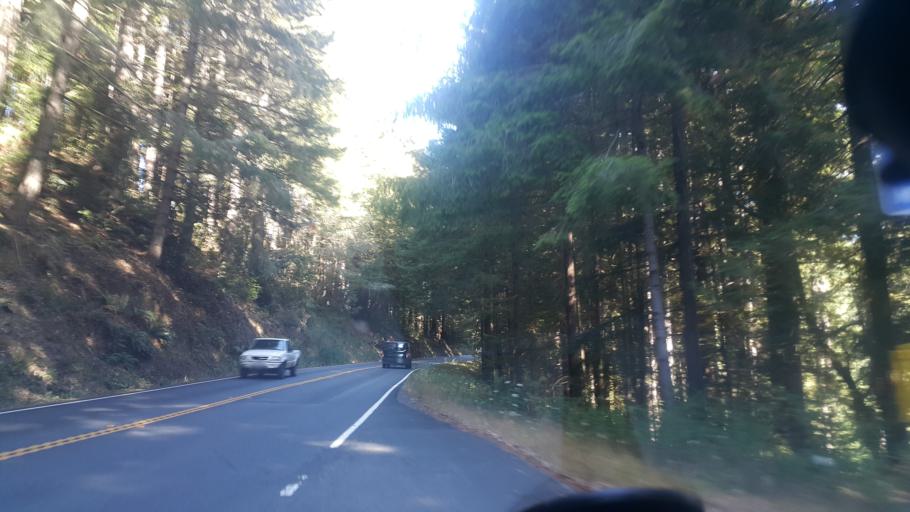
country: US
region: California
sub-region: Mendocino County
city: Fort Bragg
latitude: 39.3678
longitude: -123.6790
